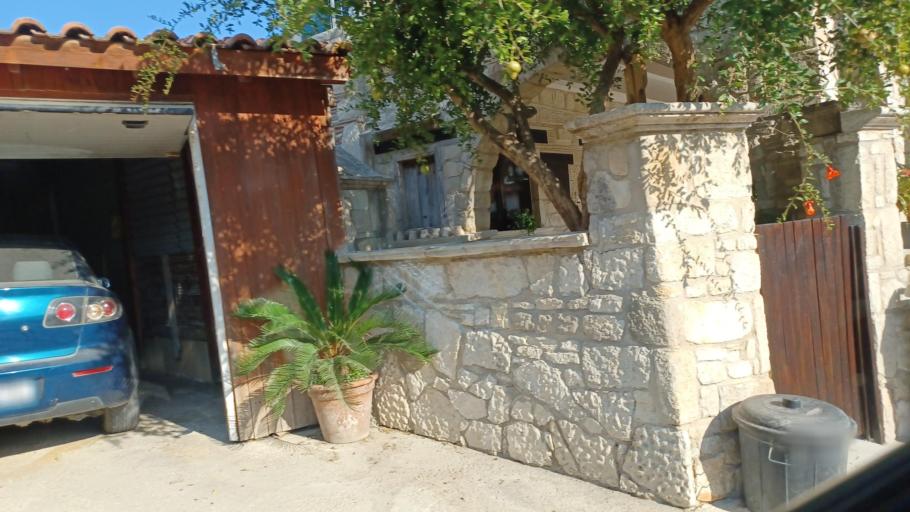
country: CY
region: Pafos
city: Mesogi
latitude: 34.8891
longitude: 32.5100
